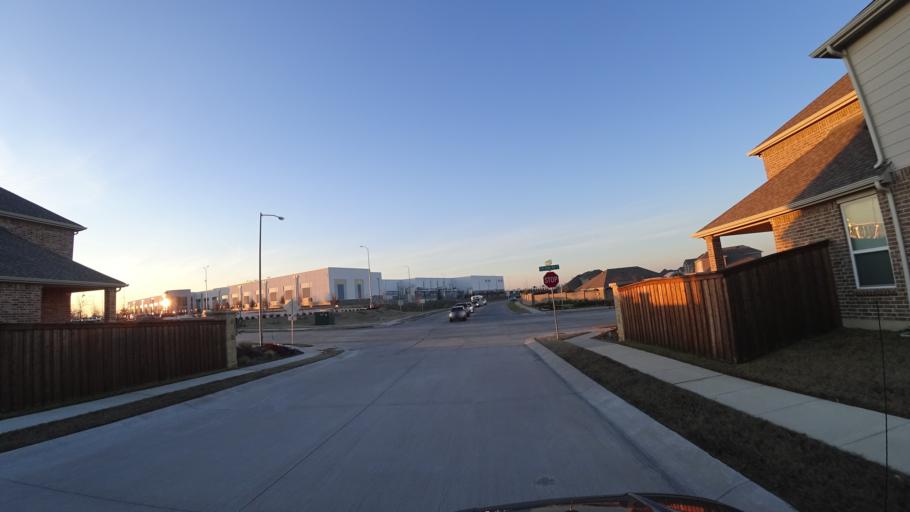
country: US
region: Texas
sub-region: Dallas County
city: Coppell
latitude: 32.9965
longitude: -96.9892
